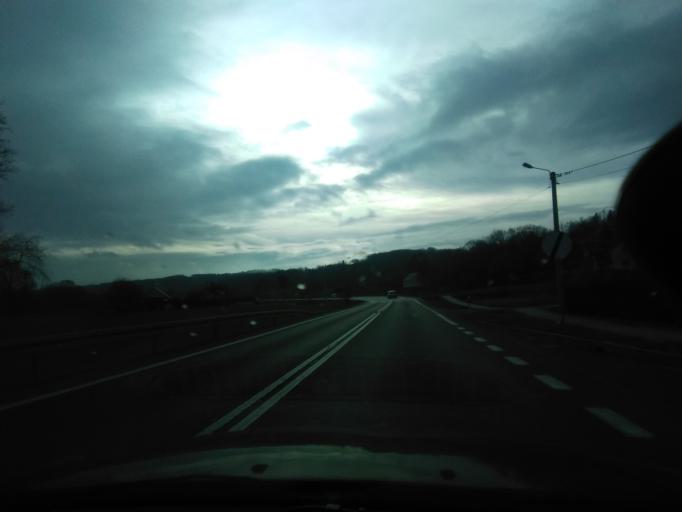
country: PL
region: Subcarpathian Voivodeship
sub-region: Powiat strzyzowski
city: Polomia
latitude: 49.9077
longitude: 21.8658
